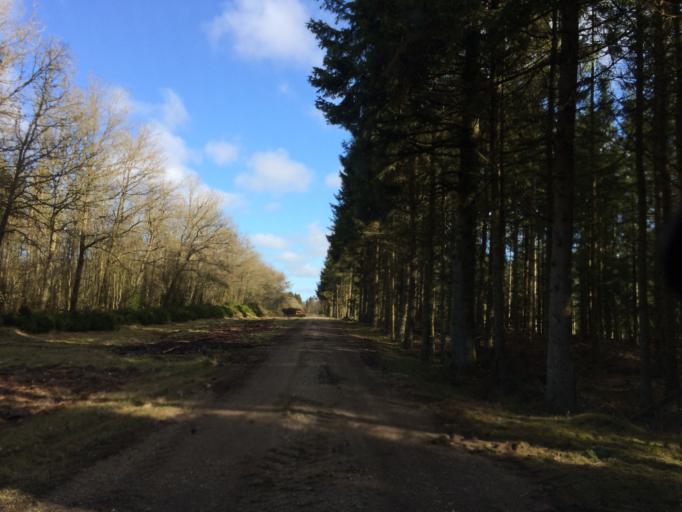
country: DK
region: Central Jutland
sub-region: Holstebro Kommune
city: Ulfborg
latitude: 56.2682
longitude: 8.4632
